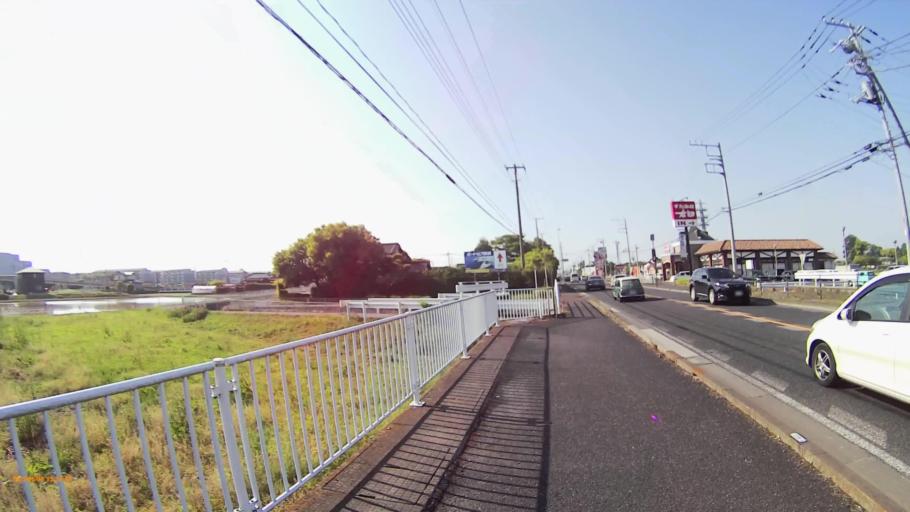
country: JP
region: Saitama
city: Sugito
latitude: 36.0450
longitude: 139.7194
